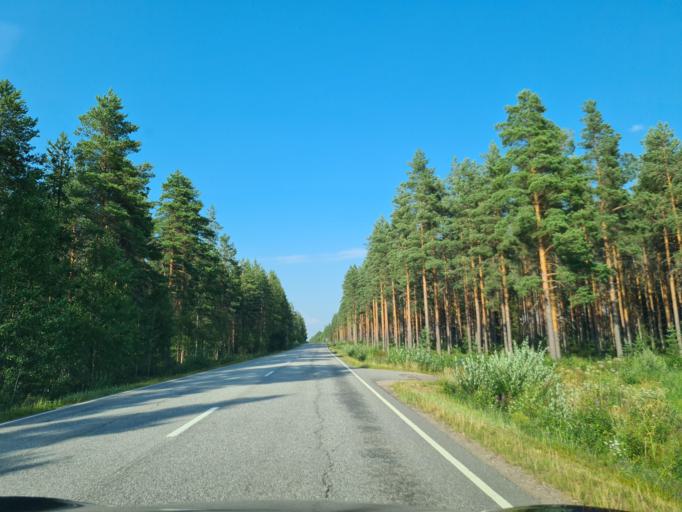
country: FI
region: Satakunta
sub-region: Pohjois-Satakunta
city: Karvia
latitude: 62.2983
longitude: 22.6294
